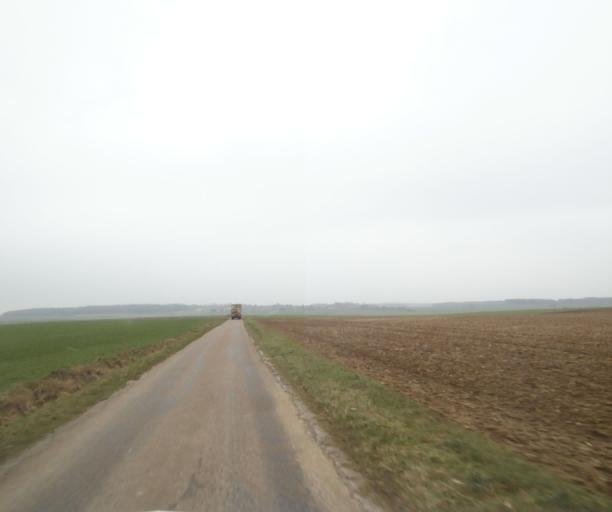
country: FR
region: Champagne-Ardenne
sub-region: Departement de la Haute-Marne
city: Chevillon
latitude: 48.5033
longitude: 5.0818
